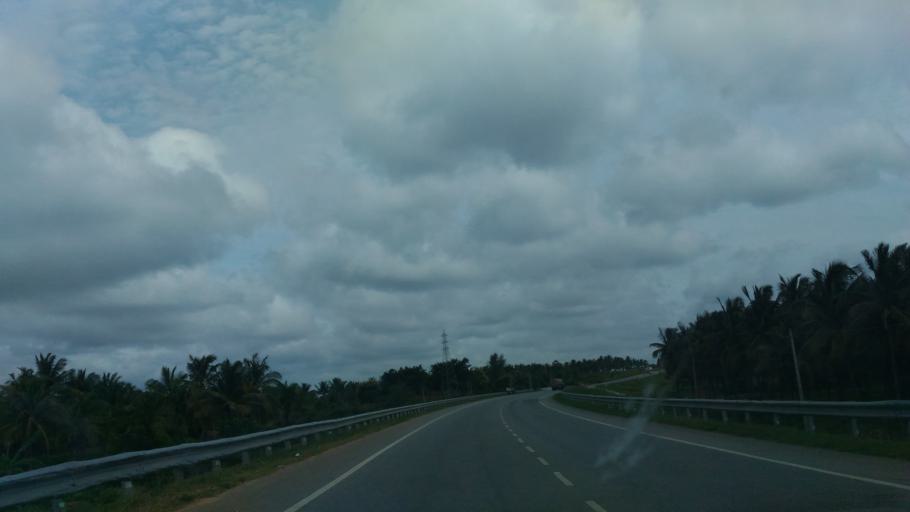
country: IN
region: Karnataka
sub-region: Hassan
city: Channarayapatna
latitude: 12.9084
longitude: 76.4221
